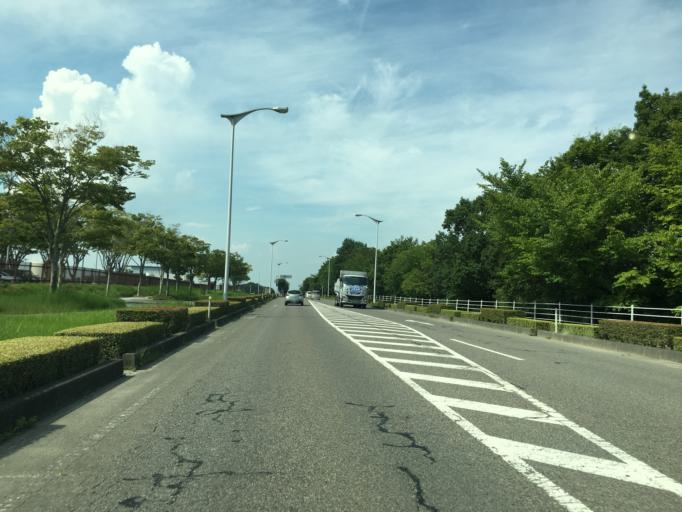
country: JP
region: Fukushima
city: Sukagawa
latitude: 37.2268
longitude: 140.4351
